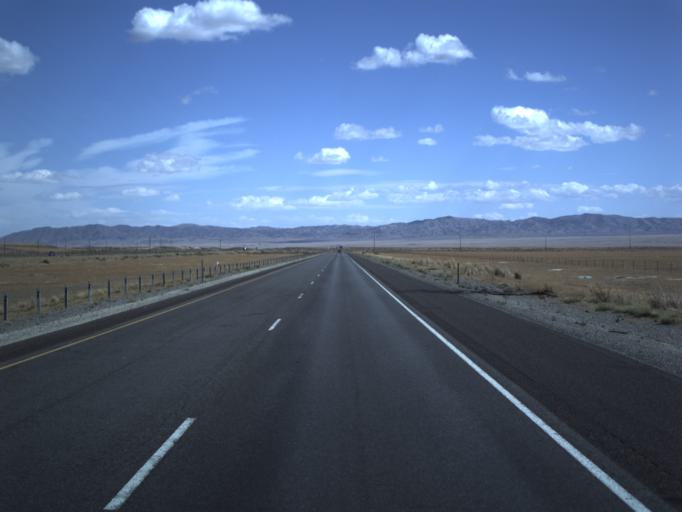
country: US
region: Utah
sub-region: Tooele County
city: Grantsville
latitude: 40.7252
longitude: -113.1516
